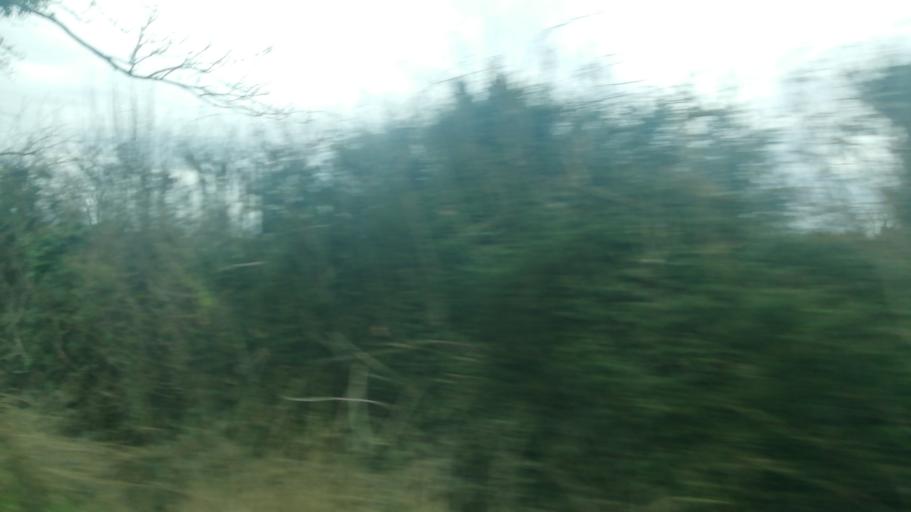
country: IE
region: Leinster
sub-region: Kildare
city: Clane
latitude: 53.3175
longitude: -6.7071
